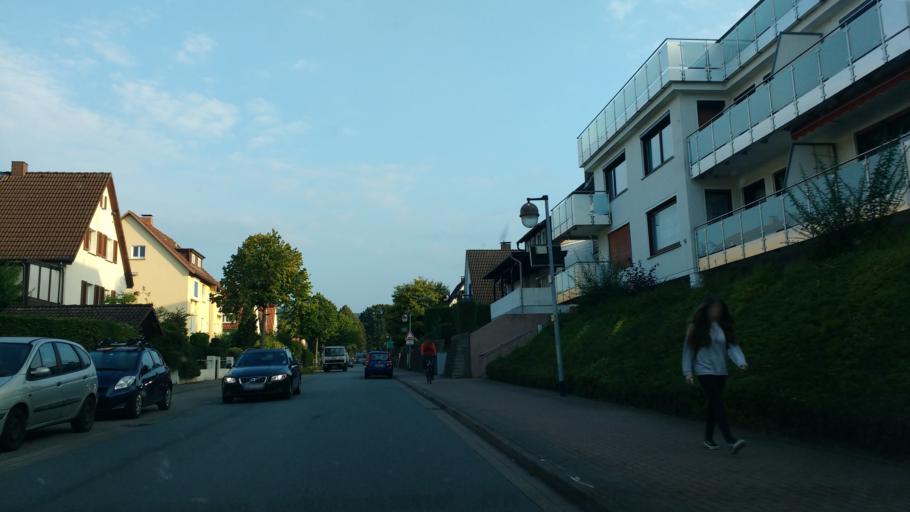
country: DE
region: Lower Saxony
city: Bad Pyrmont
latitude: 51.9799
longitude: 9.2673
